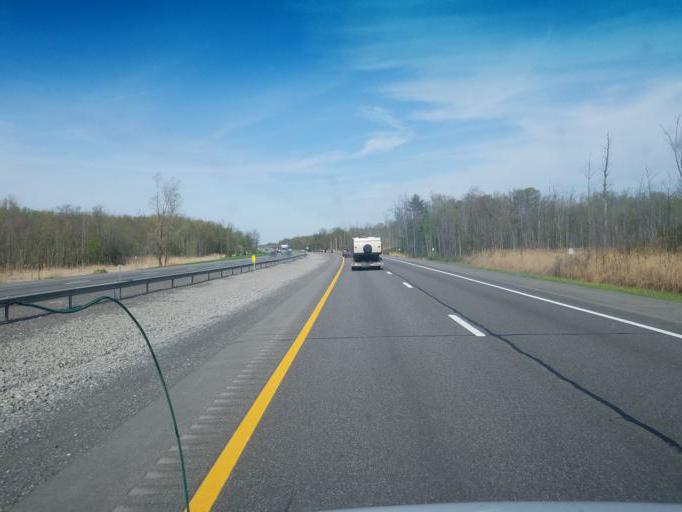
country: US
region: New York
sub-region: Madison County
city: Oneida
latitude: 43.1074
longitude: -75.6758
